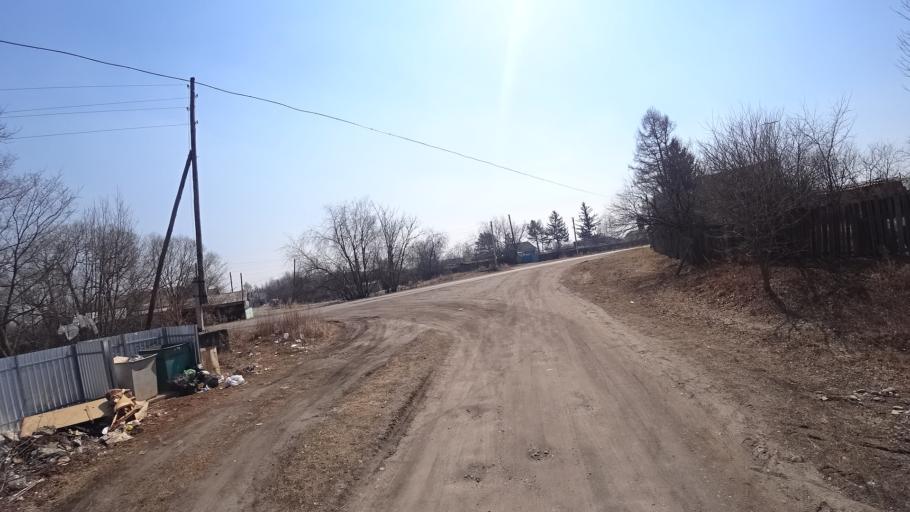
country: RU
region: Amur
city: Novobureyskiy
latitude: 49.7878
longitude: 129.8471
